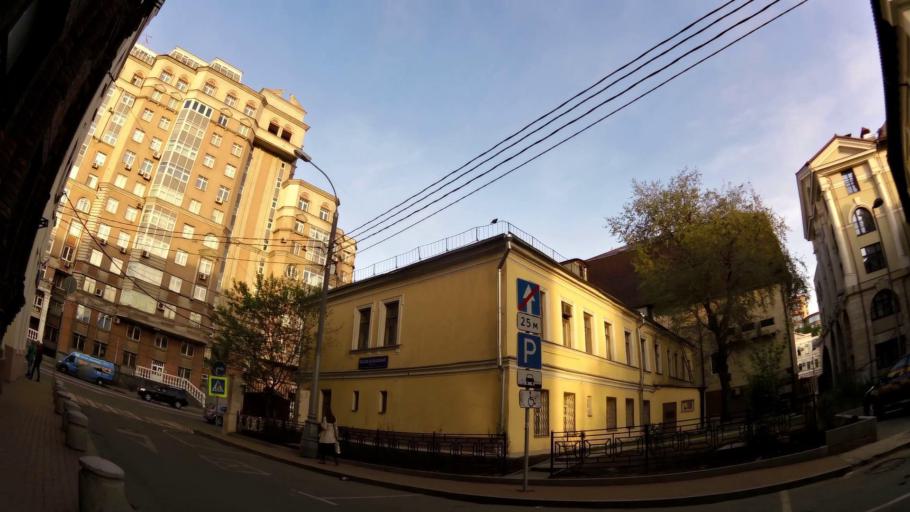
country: RU
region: Moscow
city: Moscow
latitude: 55.7761
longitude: 37.6029
